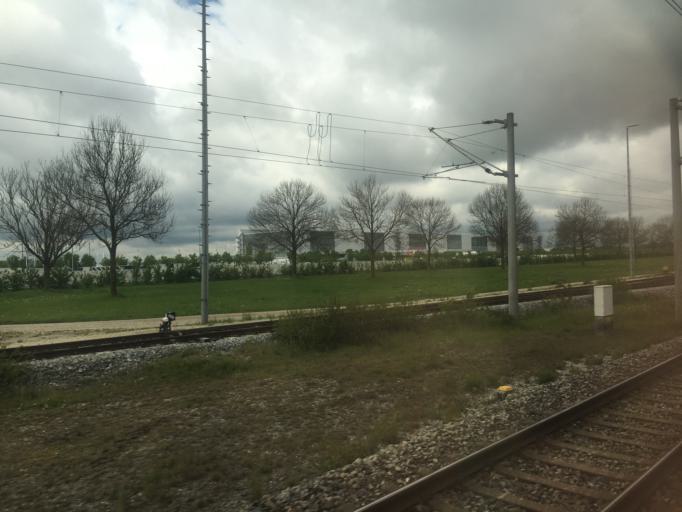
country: DE
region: Bavaria
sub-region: Upper Bavaria
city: Hallbergmoos
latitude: 48.3515
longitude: 11.7560
